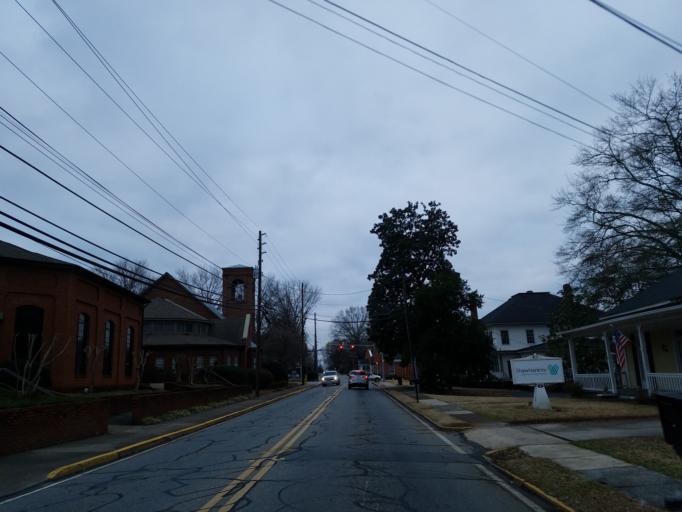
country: US
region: Georgia
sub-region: Bartow County
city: Cartersville
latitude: 34.1648
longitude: -84.8003
